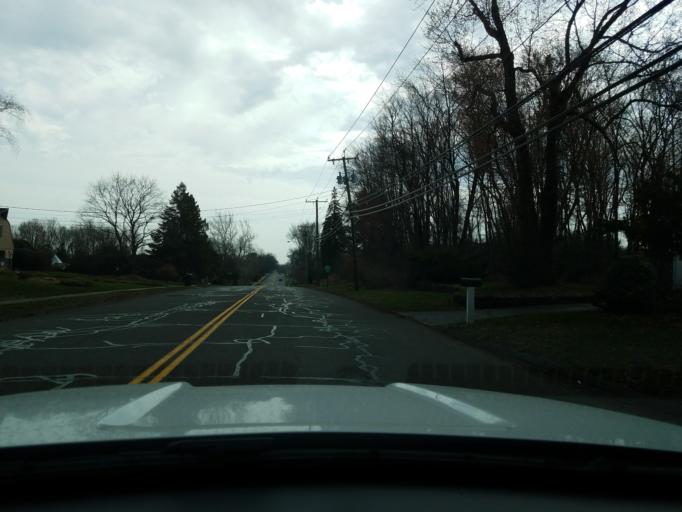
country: US
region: Connecticut
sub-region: Hartford County
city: Newington
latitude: 41.6775
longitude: -72.6899
